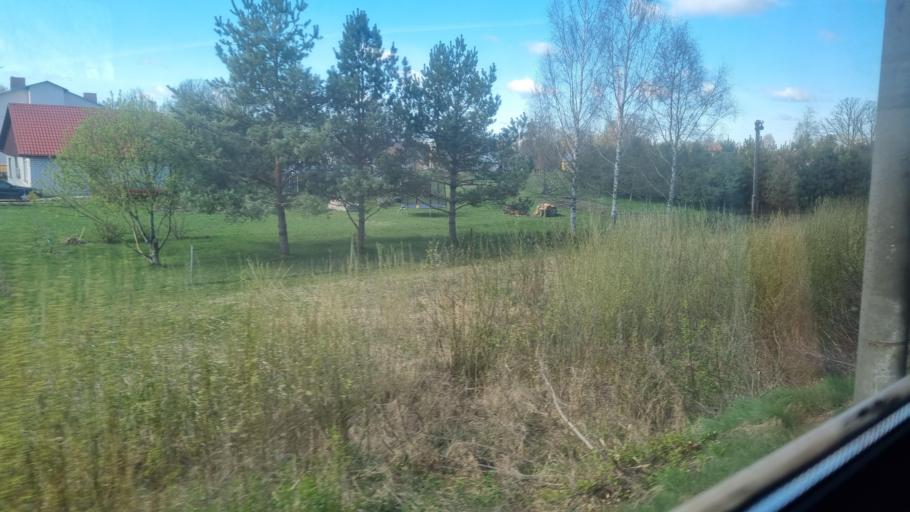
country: LV
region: Lielvarde
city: Lielvarde
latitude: 56.7184
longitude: 24.8354
